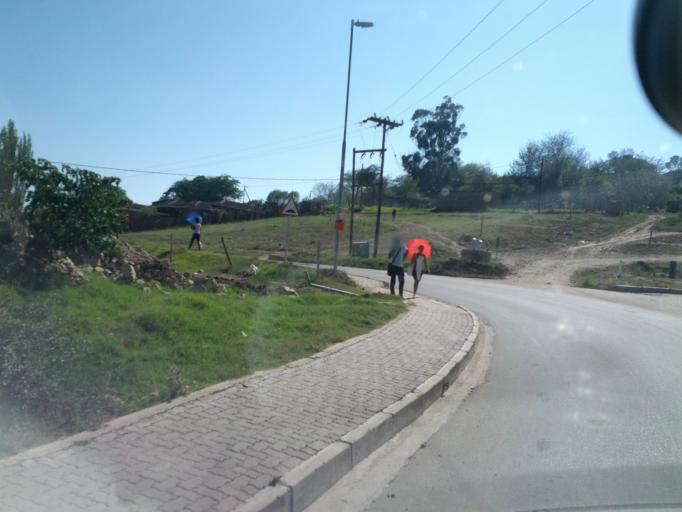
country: LS
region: Maseru
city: Maseru
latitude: -29.3038
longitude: 27.4898
